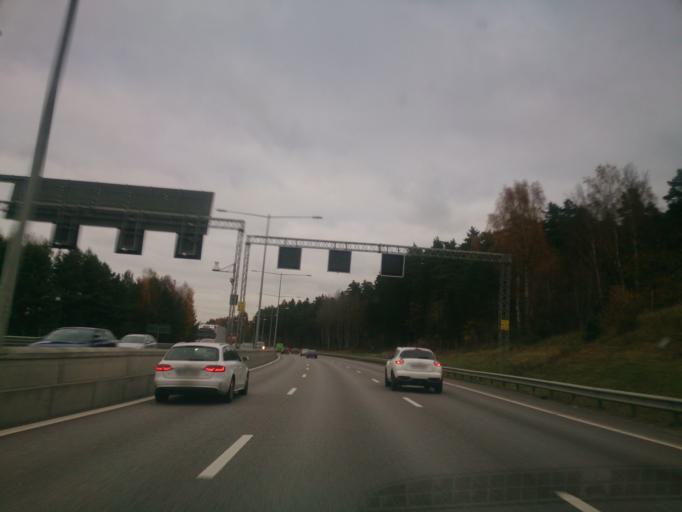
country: SE
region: Stockholm
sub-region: Botkyrka Kommun
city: Eriksberg
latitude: 59.2164
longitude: 17.7793
